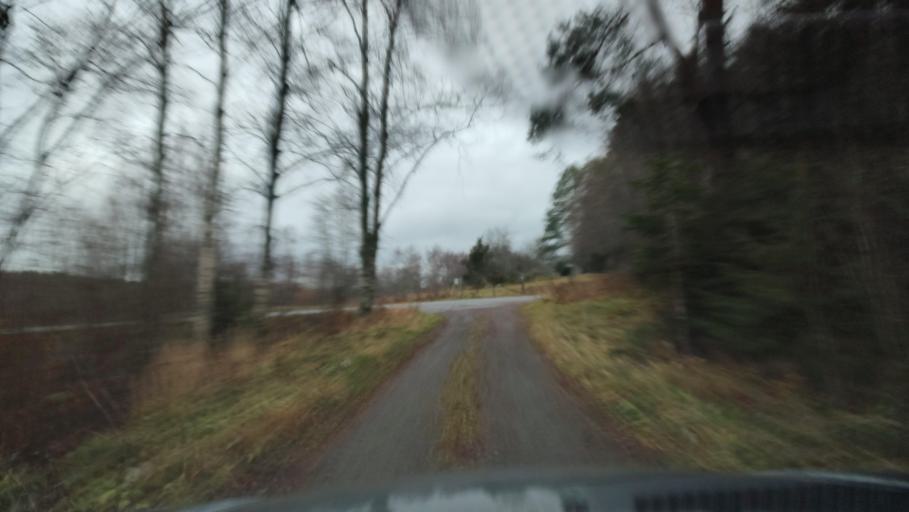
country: FI
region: Ostrobothnia
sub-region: Sydosterbotten
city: Kristinestad
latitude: 62.2802
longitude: 21.4106
